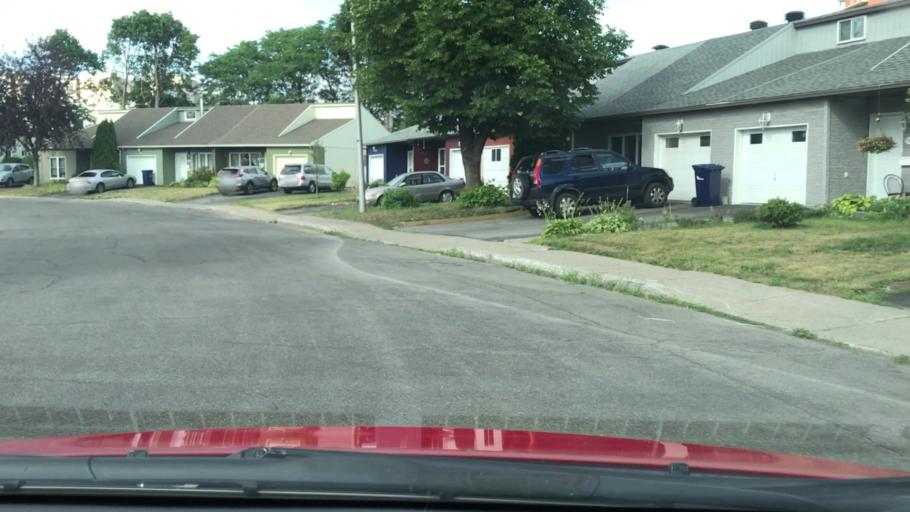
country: CA
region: Quebec
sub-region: Laval
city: Laval
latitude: 45.5472
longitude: -73.7389
